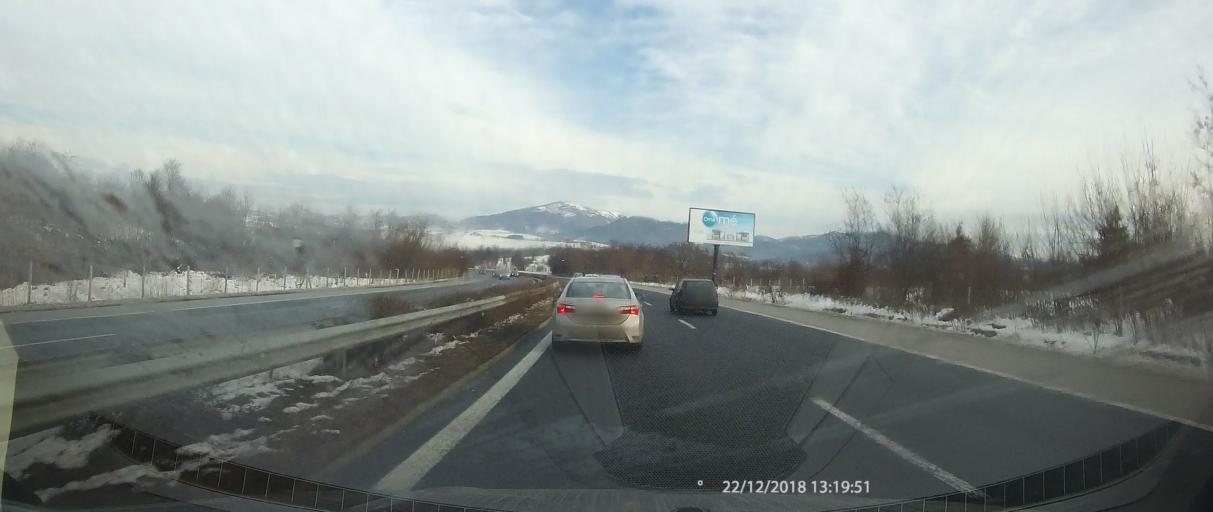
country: BG
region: Sofiya
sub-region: Obshtina Pravets
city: Pravets
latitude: 42.9480
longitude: 24.0095
